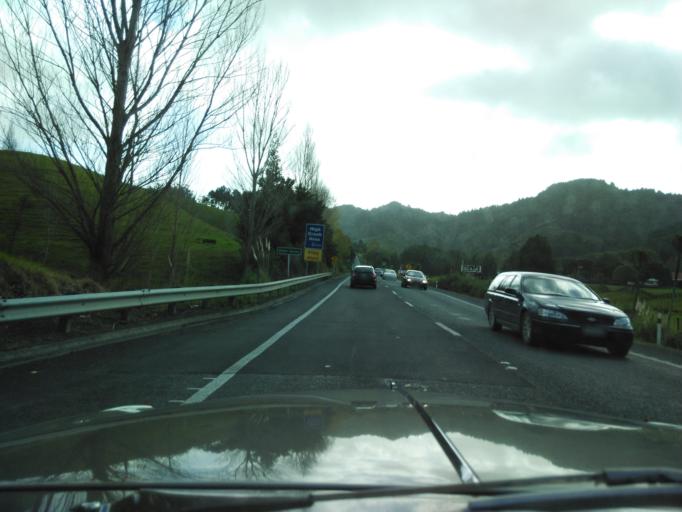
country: NZ
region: Auckland
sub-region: Auckland
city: Warkworth
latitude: -36.3735
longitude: 174.6300
